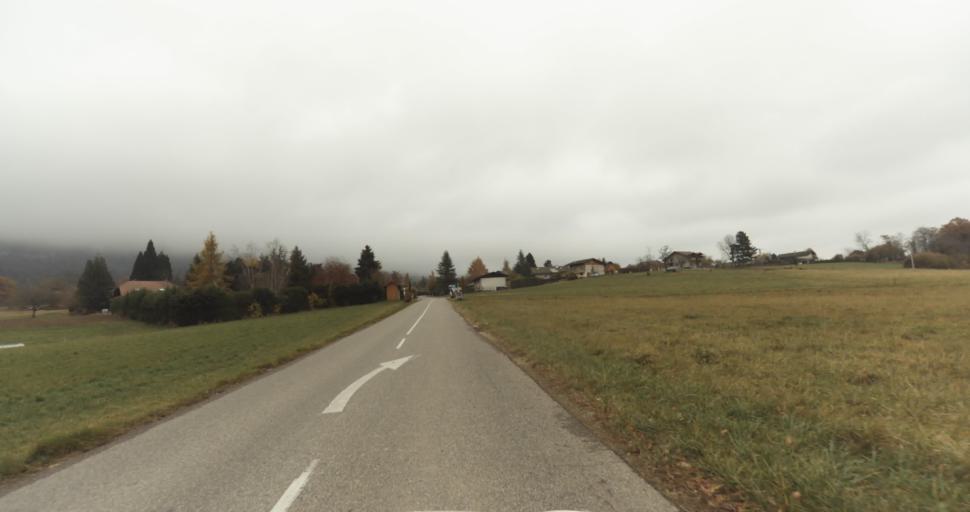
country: FR
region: Rhone-Alpes
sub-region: Departement de la Haute-Savoie
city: Seynod
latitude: 45.8504
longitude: 6.0845
